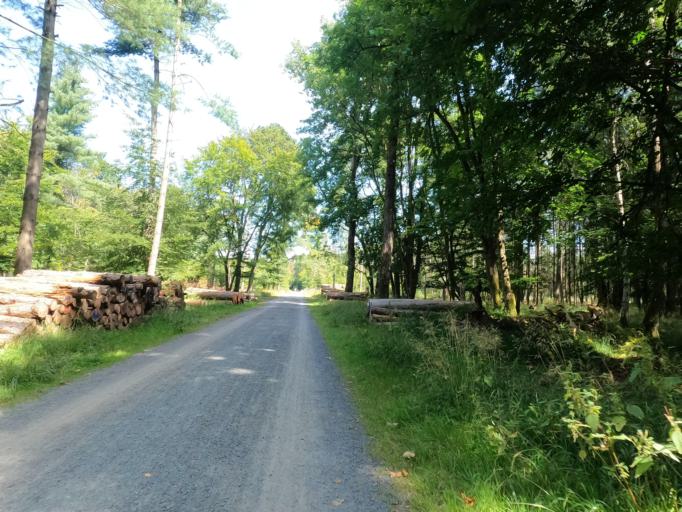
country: DE
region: Hesse
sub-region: Regierungsbezirk Darmstadt
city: Neu Isenburg
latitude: 50.0679
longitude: 8.7119
